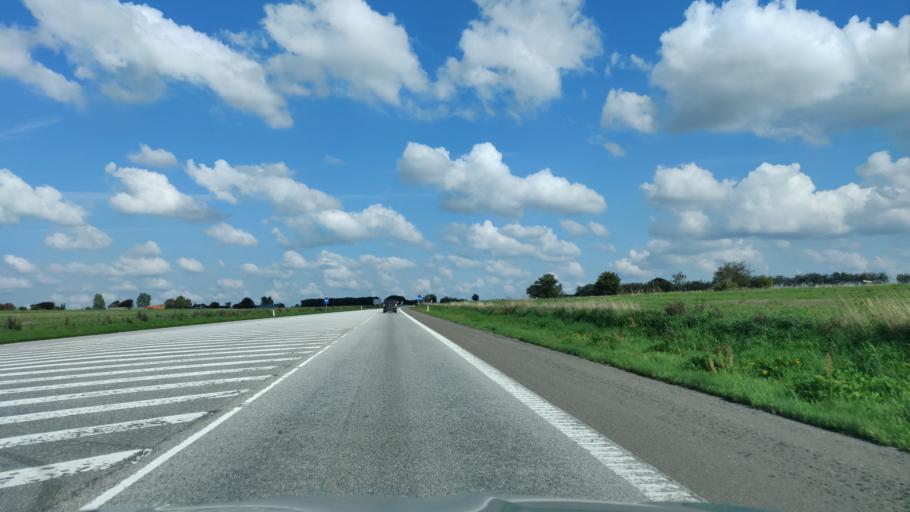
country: DK
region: North Denmark
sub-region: Vesthimmerland Kommune
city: Aars
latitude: 56.8090
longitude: 9.6532
